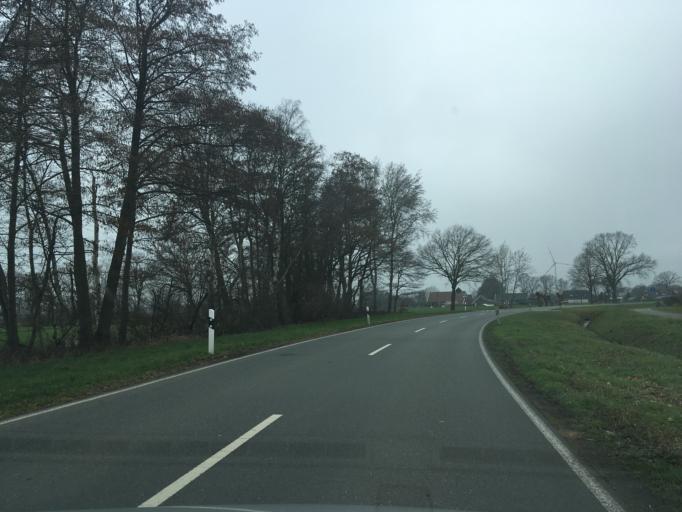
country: DE
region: North Rhine-Westphalia
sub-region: Regierungsbezirk Dusseldorf
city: Bocholt
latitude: 51.8788
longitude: 6.5980
